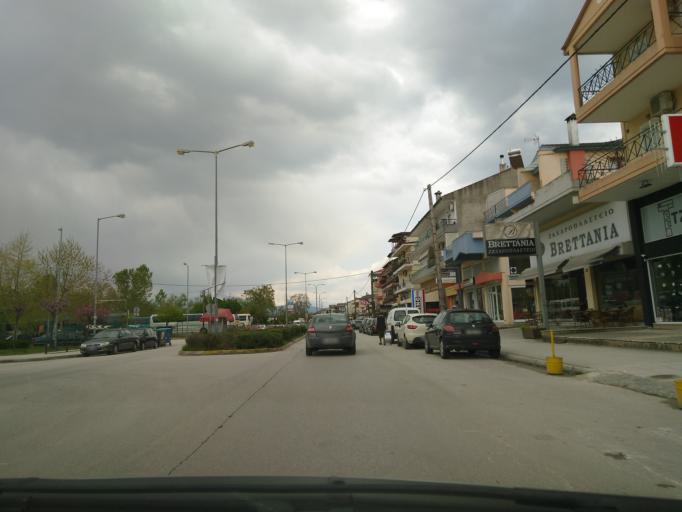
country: GR
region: Epirus
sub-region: Nomos Ioanninon
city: Ioannina
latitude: 39.6742
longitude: 20.8470
